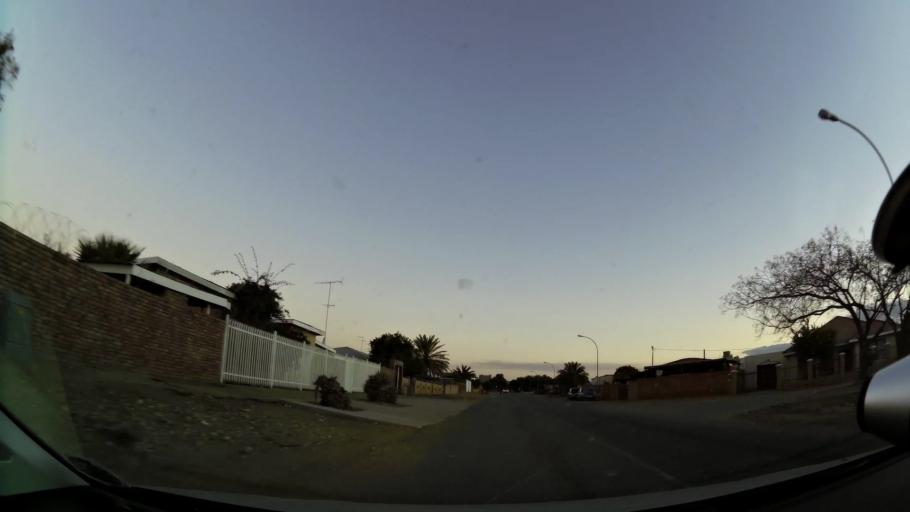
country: ZA
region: Northern Cape
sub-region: Frances Baard District Municipality
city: Kimberley
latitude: -28.7207
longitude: 24.7676
